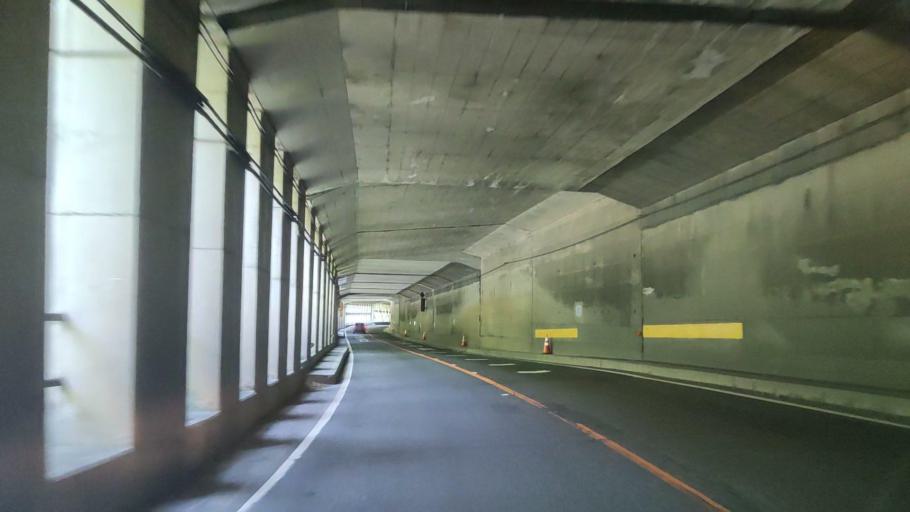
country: JP
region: Niigata
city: Itoigawa
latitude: 36.9034
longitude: 137.8686
